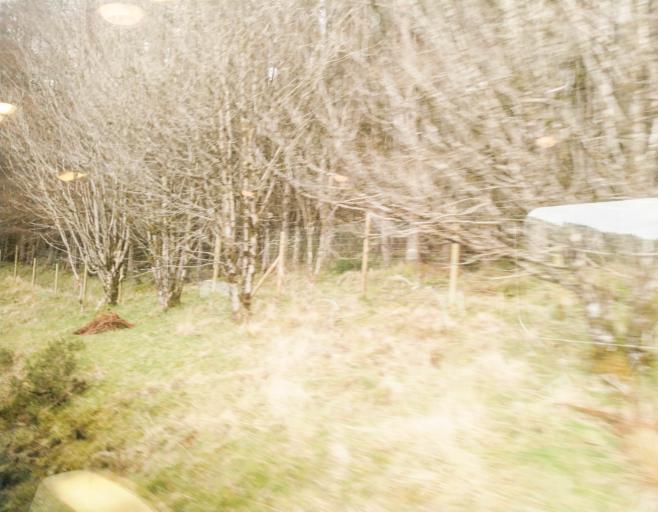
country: GB
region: Scotland
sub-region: Argyll and Bute
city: Garelochhead
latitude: 56.4430
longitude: -4.7079
